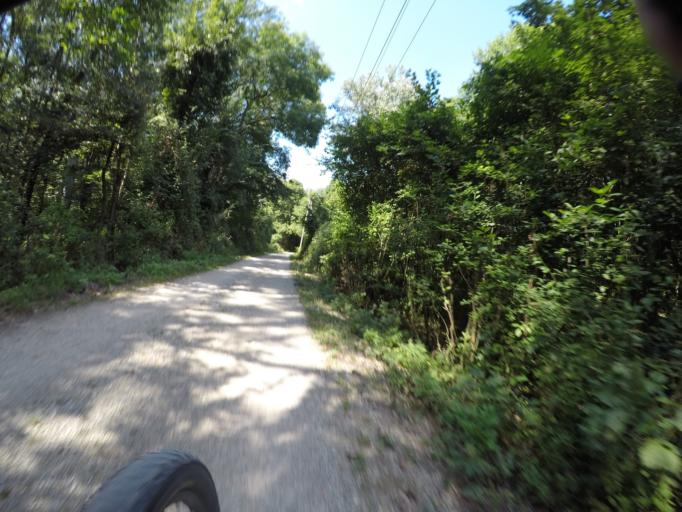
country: AT
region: Lower Austria
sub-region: Politischer Bezirk Ganserndorf
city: Gross-Enzersdorf
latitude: 48.1776
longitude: 16.5261
